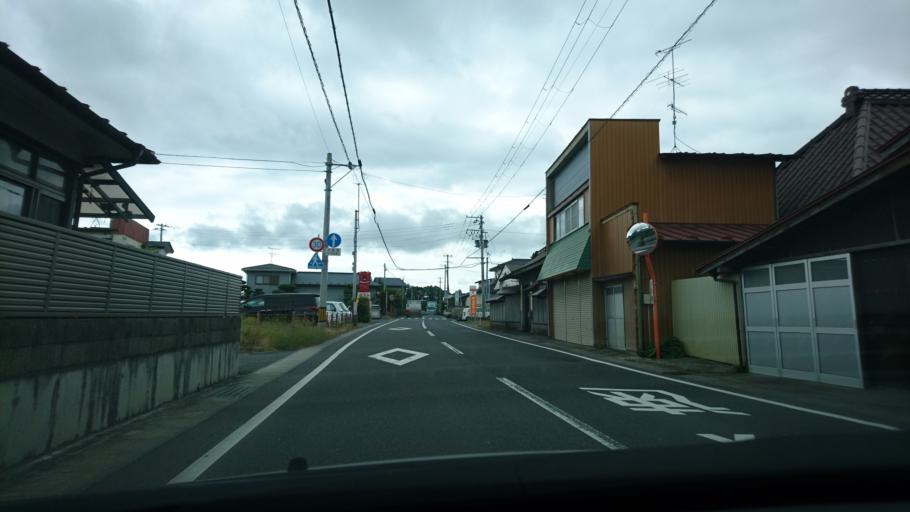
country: JP
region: Miyagi
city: Wakuya
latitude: 38.7292
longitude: 141.2602
